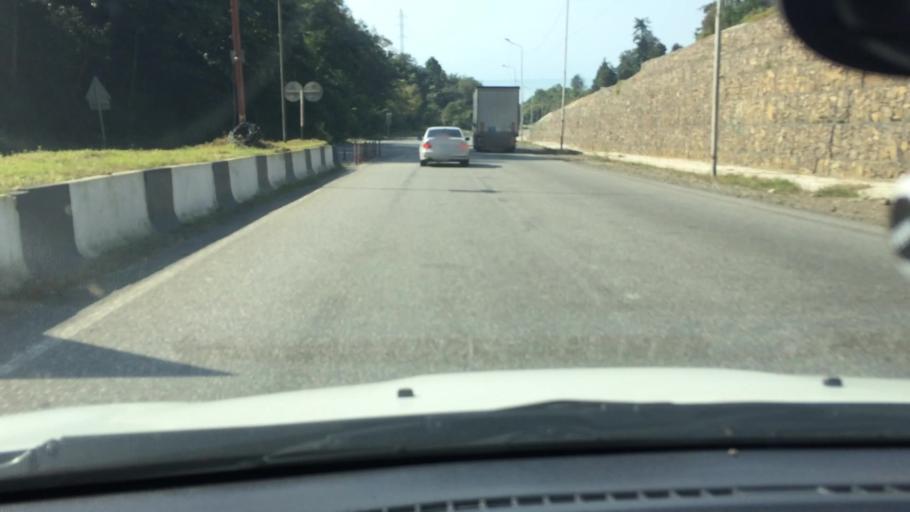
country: GE
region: Ajaria
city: Makhinjauri
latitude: 41.6901
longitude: 41.7167
